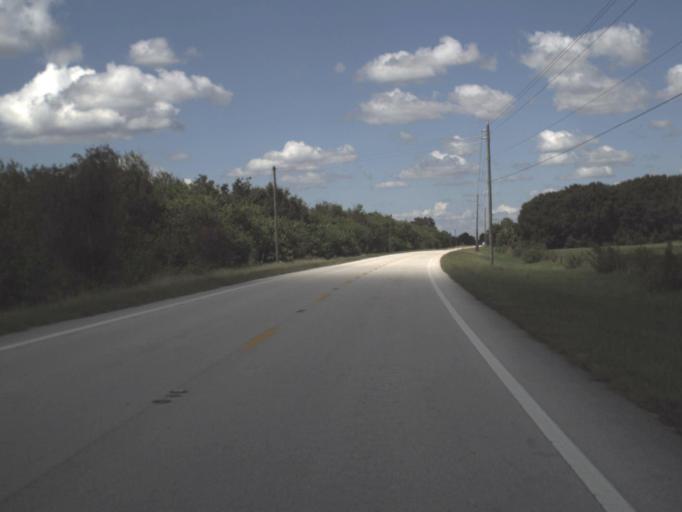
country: US
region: Florida
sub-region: Okeechobee County
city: Taylor Creek
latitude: 27.1249
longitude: -80.6802
